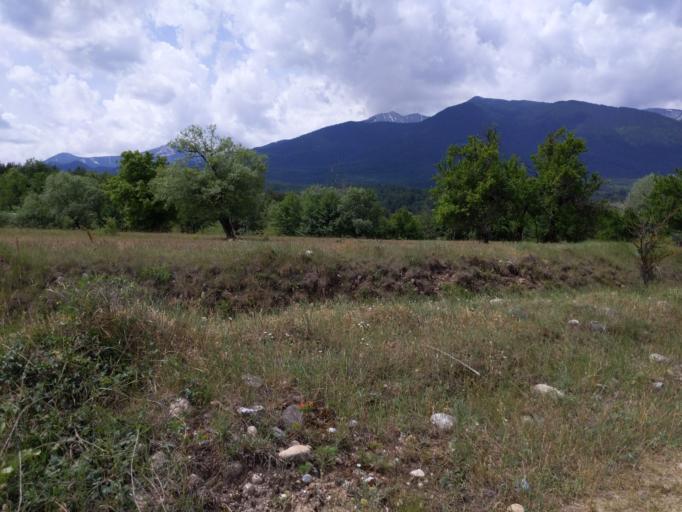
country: BG
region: Blagoevgrad
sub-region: Obshtina Bansko
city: Bansko
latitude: 41.8444
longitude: 23.4589
